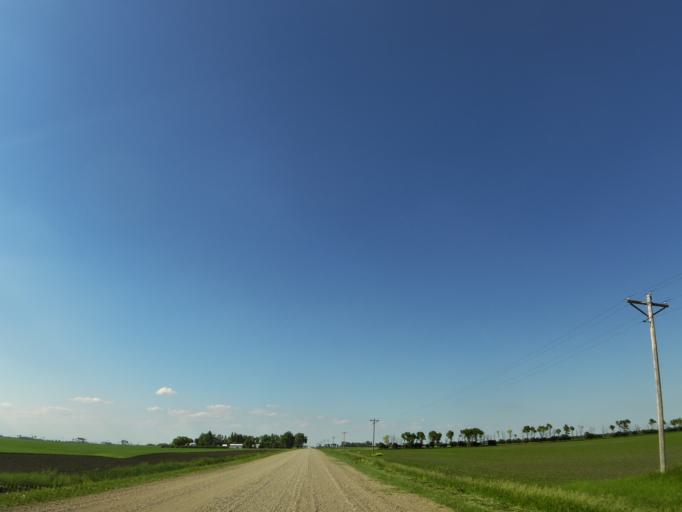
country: US
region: North Dakota
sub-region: Walsh County
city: Grafton
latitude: 48.3142
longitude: -97.2552
